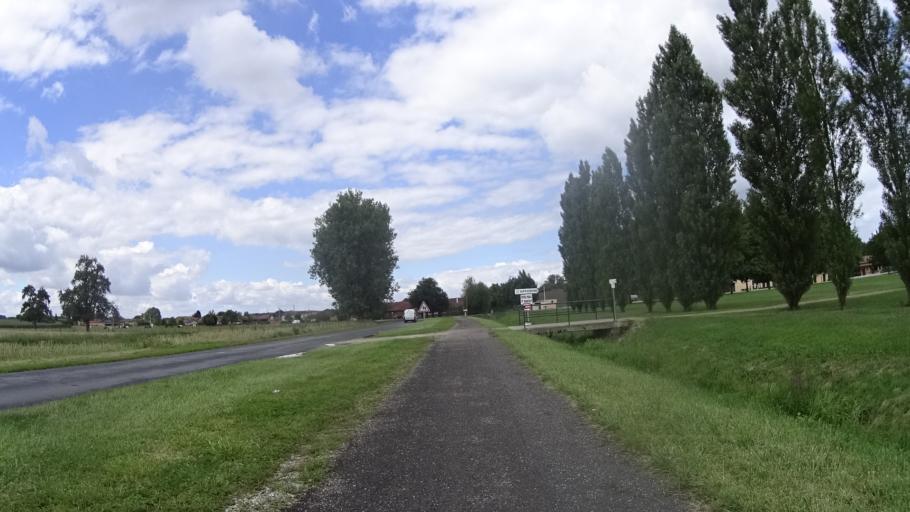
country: FR
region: Champagne-Ardenne
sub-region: Departement de la Haute-Marne
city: Montier-en-Der
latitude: 48.4768
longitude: 4.7612
